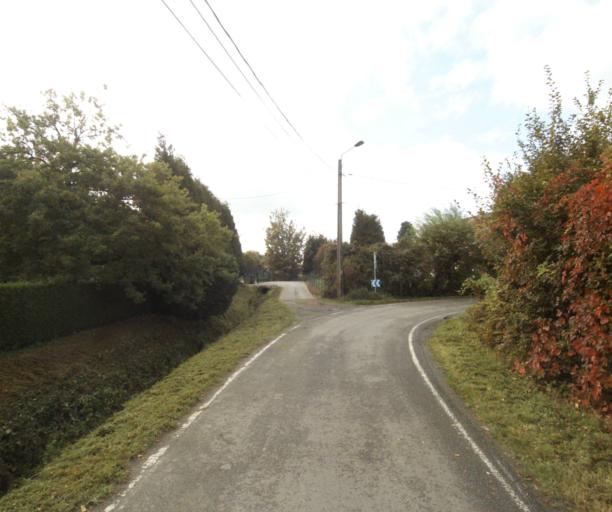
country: FR
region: Nord-Pas-de-Calais
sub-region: Departement du Nord
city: Verlinghem
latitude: 50.6720
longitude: 3.0196
